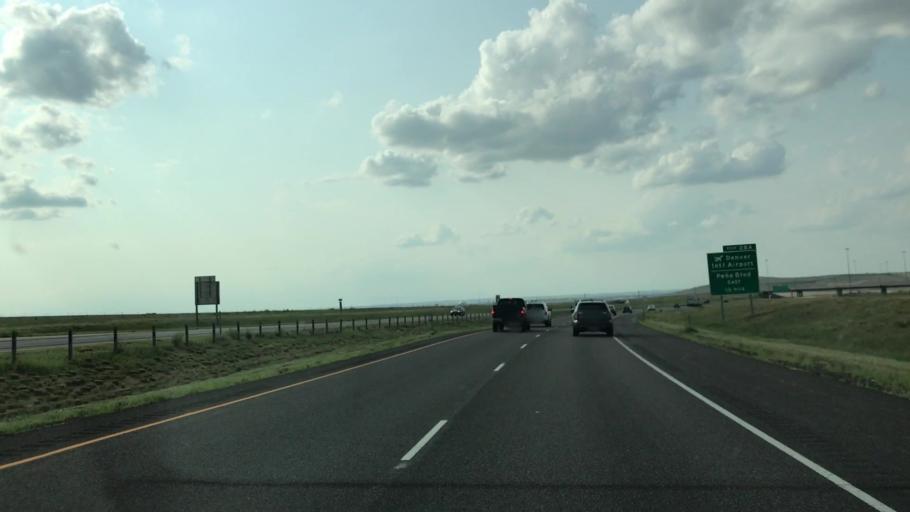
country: US
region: Colorado
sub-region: Adams County
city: Aurora
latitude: 39.8213
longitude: -104.7434
